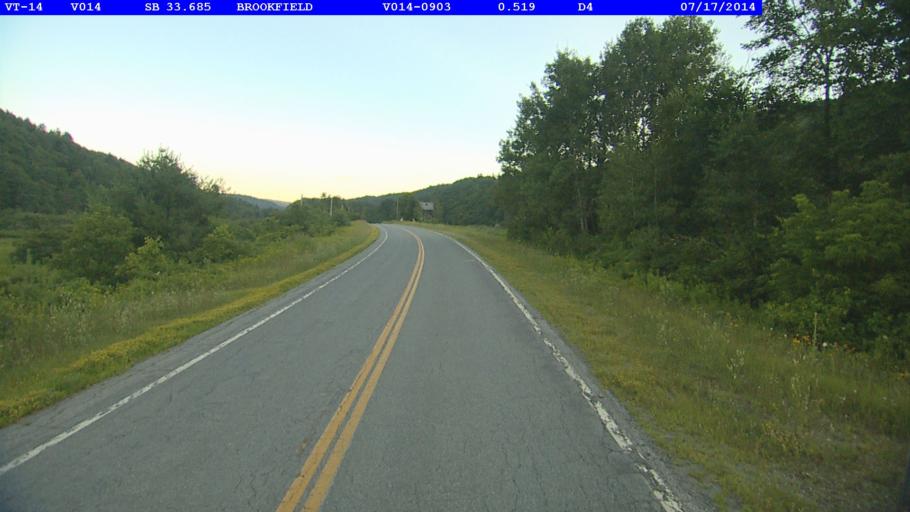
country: US
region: Vermont
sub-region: Orange County
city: Chelsea
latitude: 43.9865
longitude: -72.5571
